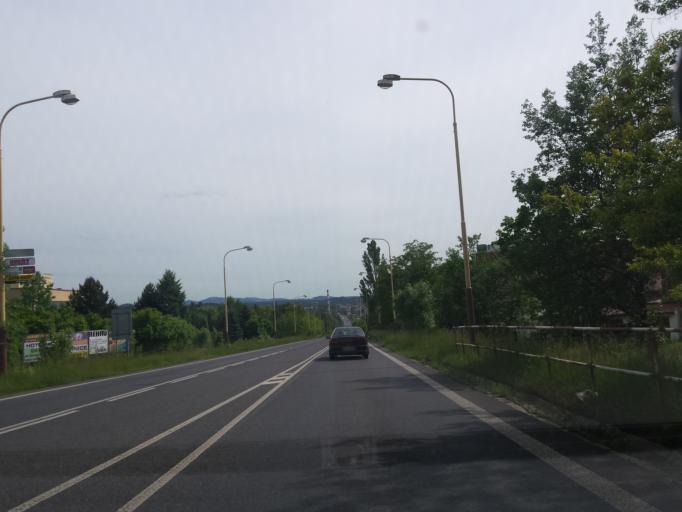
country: CZ
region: Liberecky
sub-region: Okres Ceska Lipa
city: Ceska Lipa
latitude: 50.6911
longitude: 14.5415
